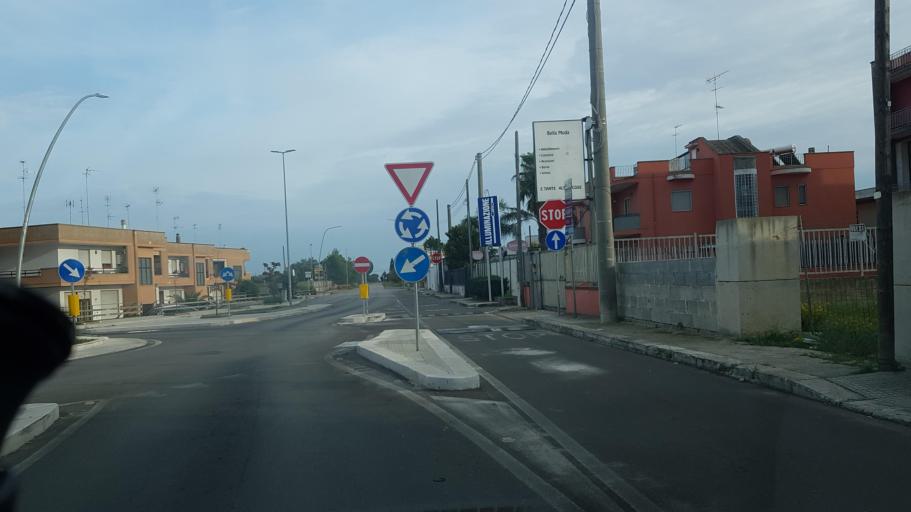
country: IT
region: Apulia
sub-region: Provincia di Lecce
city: Trepuzzi
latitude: 40.3992
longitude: 18.0828
